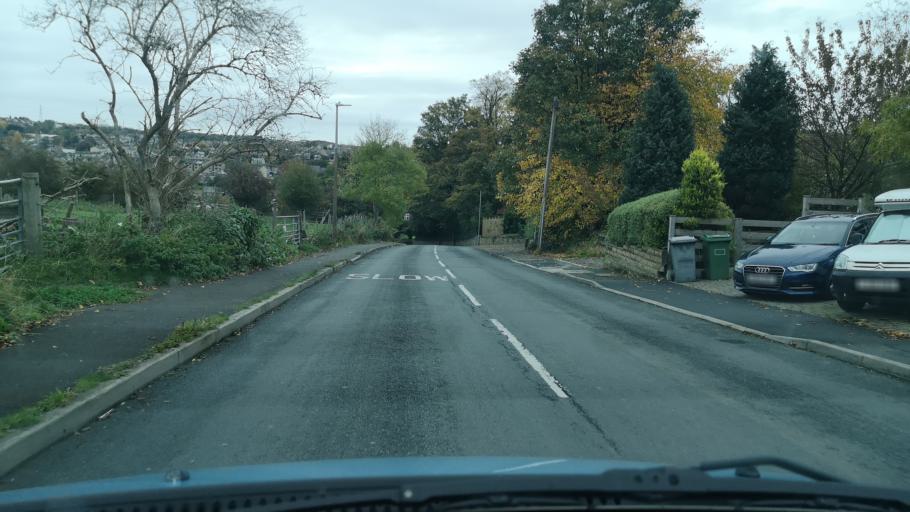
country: GB
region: England
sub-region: Kirklees
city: Heckmondwike
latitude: 53.7239
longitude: -1.6619
